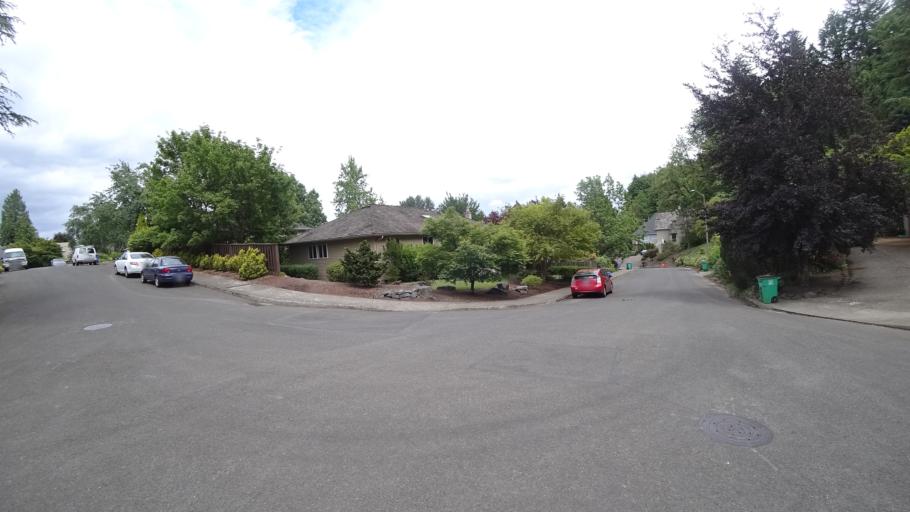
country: US
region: Oregon
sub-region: Clackamas County
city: Lake Oswego
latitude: 45.4522
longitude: -122.6983
